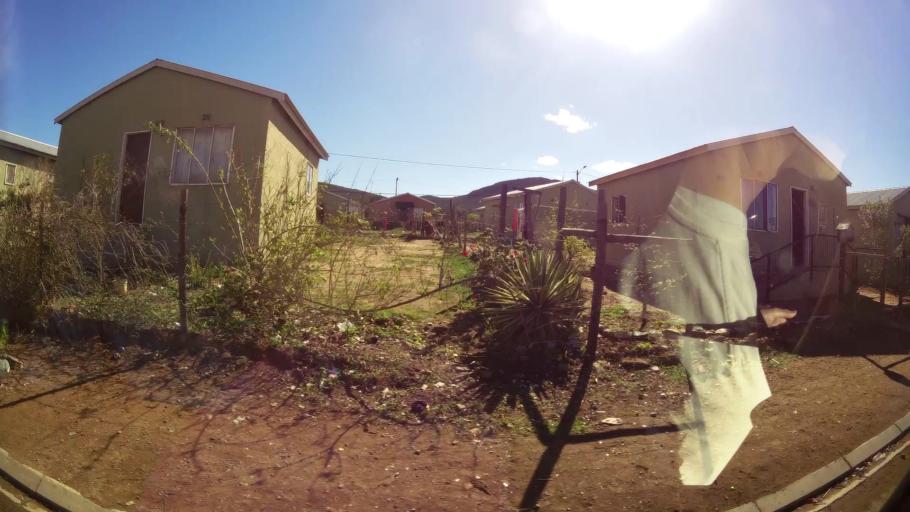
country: ZA
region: Western Cape
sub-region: Cape Winelands District Municipality
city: Ashton
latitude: -33.7710
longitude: 20.1416
